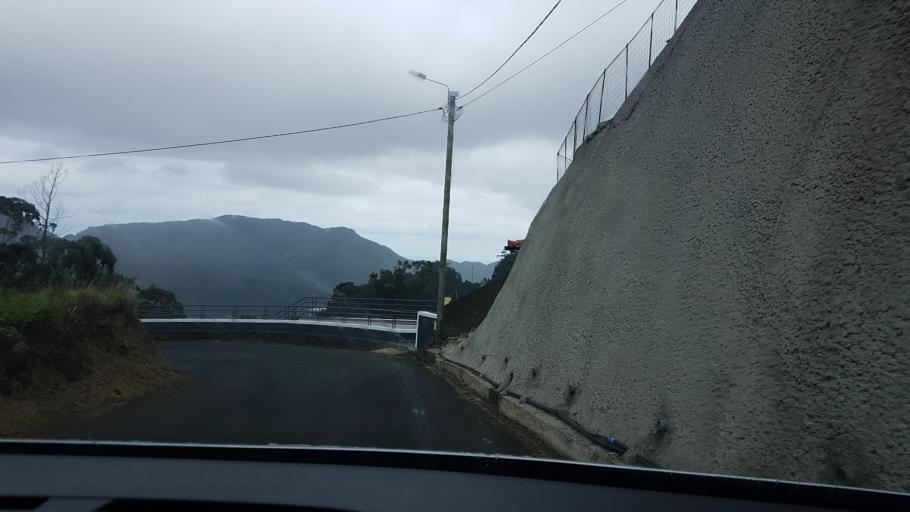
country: PT
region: Madeira
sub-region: Santa Cruz
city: Santa Cruz
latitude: 32.7291
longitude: -16.8084
